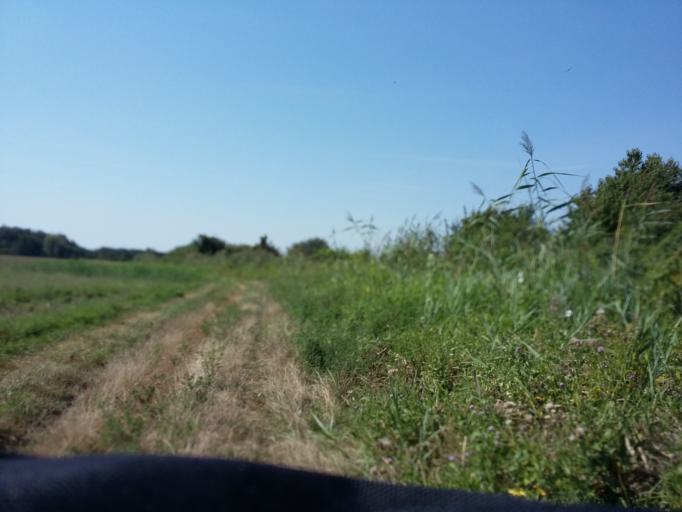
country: SK
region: Bratislavsky
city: Stupava
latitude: 48.3244
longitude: 17.0386
